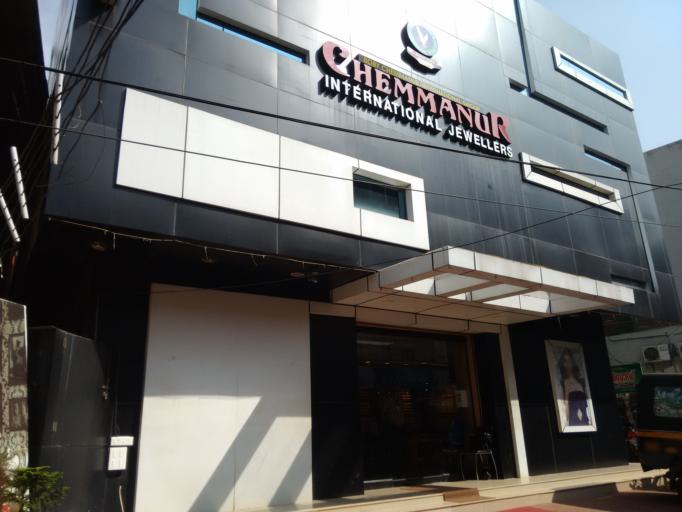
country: IN
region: Kerala
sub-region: Kozhikode
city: Badagara
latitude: 11.5985
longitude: 75.5886
